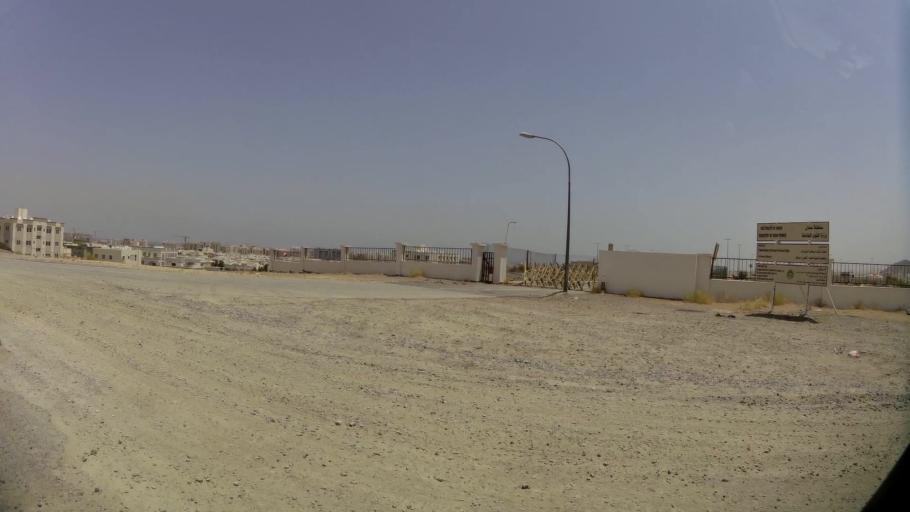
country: OM
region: Muhafazat Masqat
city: Bawshar
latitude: 23.5750
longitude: 58.4275
